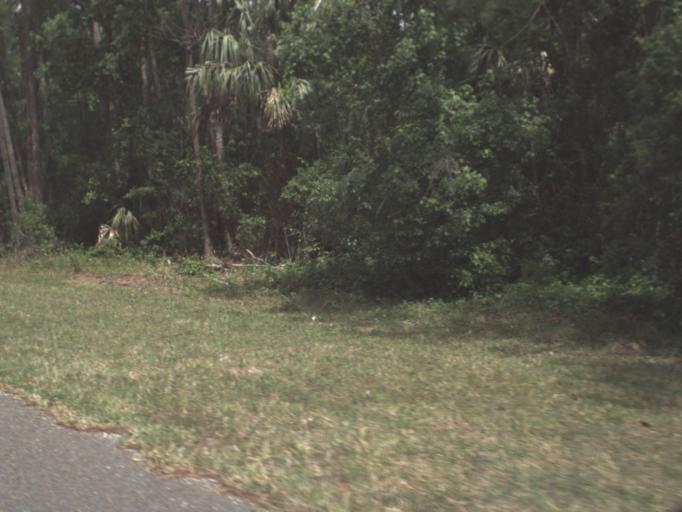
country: US
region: Florida
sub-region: Volusia County
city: Pierson
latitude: 29.2728
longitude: -81.3364
